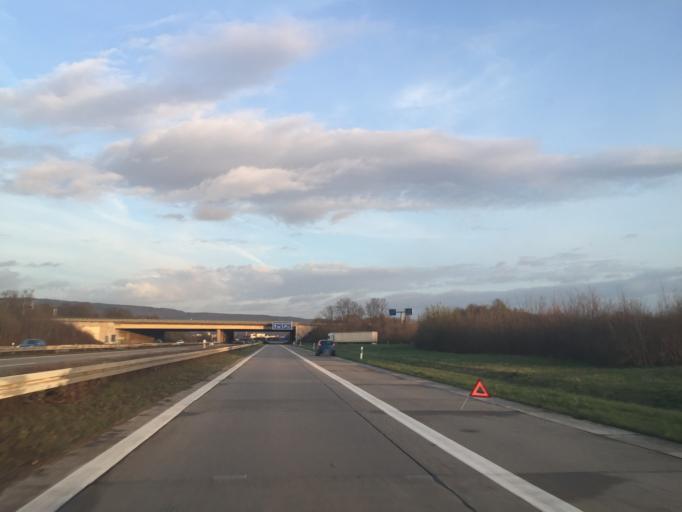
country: DE
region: Baden-Wuerttemberg
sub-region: Karlsruhe Region
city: Eppelheim
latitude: 49.4197
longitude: 8.6306
